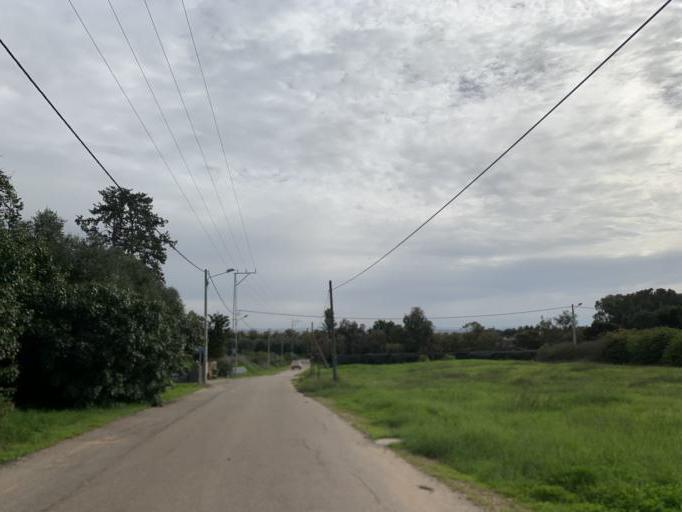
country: IL
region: Central District
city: Hod HaSharon
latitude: 32.1499
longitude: 34.9044
